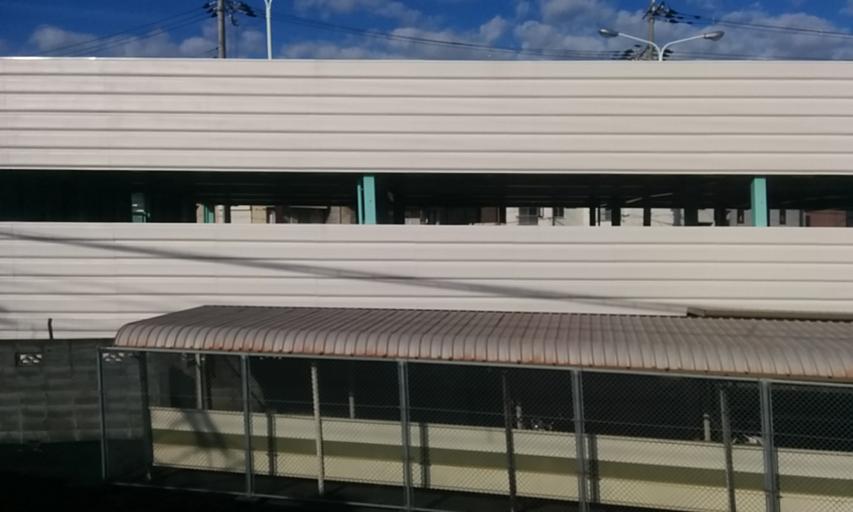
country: JP
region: Kyoto
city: Uji
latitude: 34.8920
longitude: 135.7816
